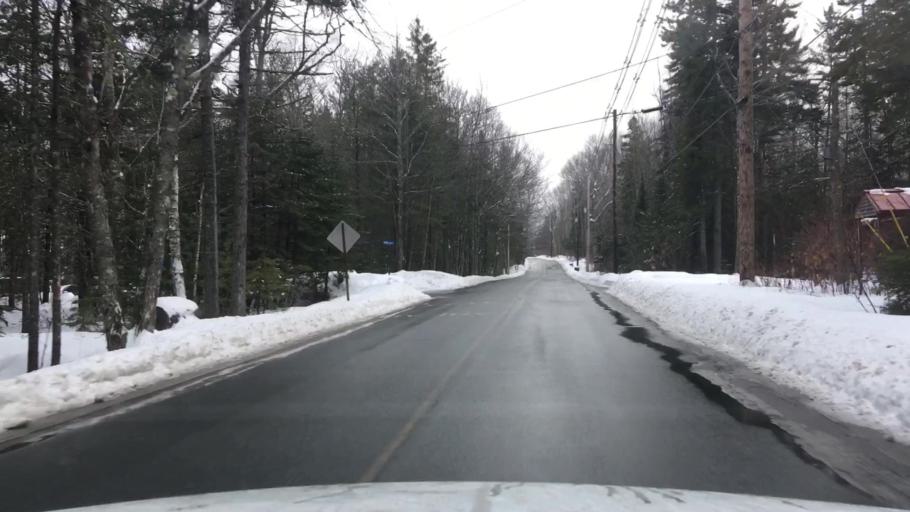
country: US
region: Maine
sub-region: Hancock County
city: Trenton
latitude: 44.4195
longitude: -68.3337
